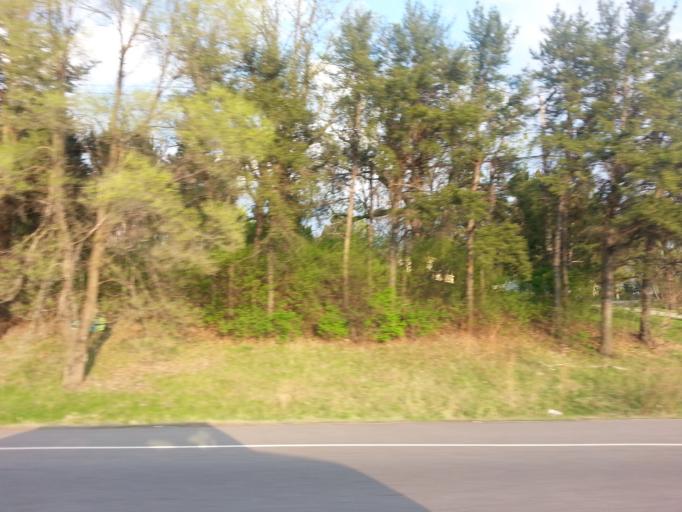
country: US
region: Minnesota
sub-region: Dakota County
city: Eagan
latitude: 44.8381
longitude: -93.1884
